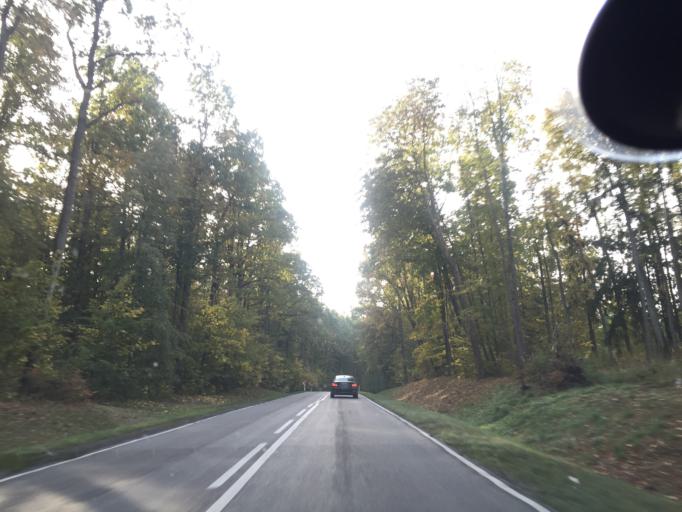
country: PL
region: Warmian-Masurian Voivodeship
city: Dobre Miasto
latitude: 54.0103
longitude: 20.4135
